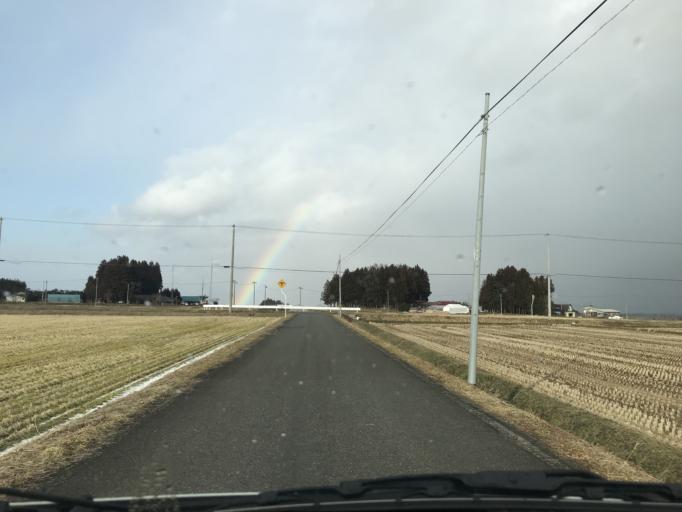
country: JP
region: Iwate
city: Mizusawa
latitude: 39.0920
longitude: 141.0300
